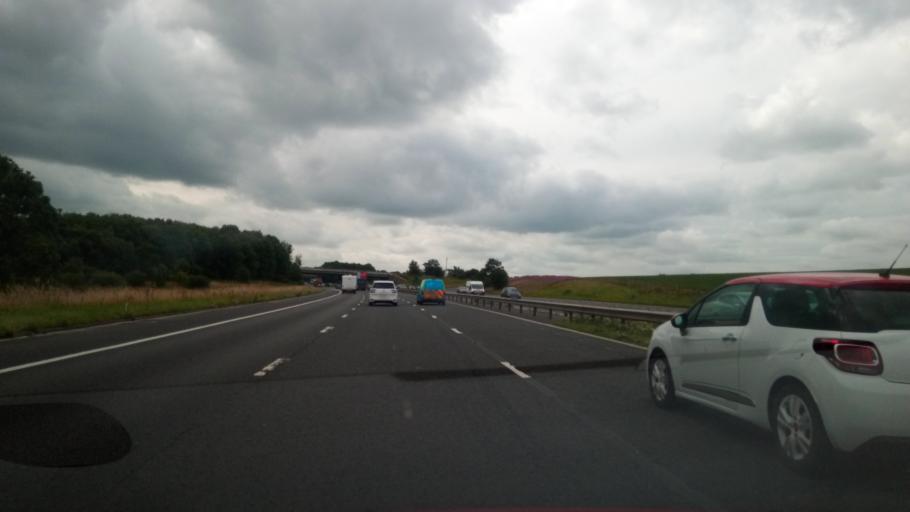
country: GB
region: England
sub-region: Lancashire
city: Galgate
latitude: 53.9857
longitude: -2.7813
